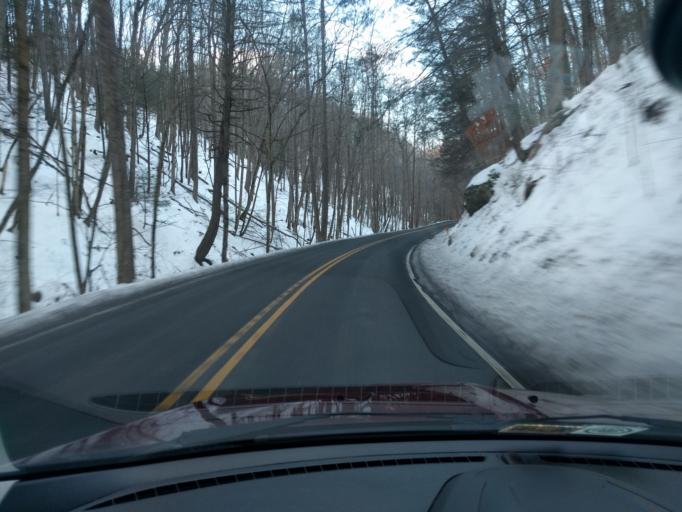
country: US
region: Virginia
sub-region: Bath County
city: Warm Springs
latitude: 38.0734
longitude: -79.8767
